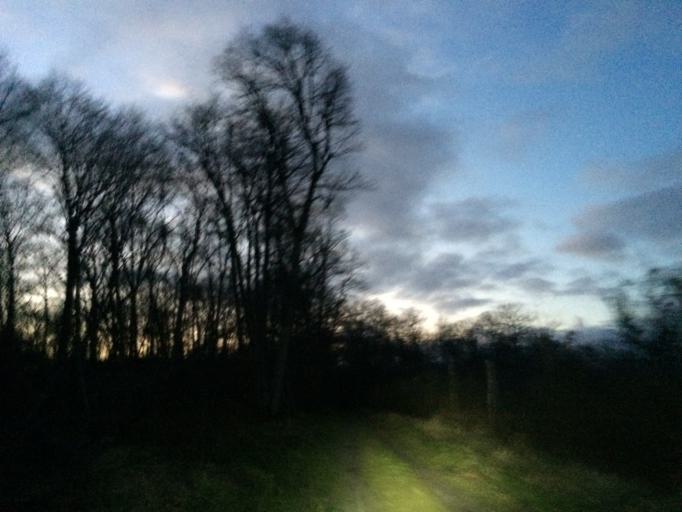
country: FR
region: Picardie
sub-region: Departement de l'Oise
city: Coye-la-Foret
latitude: 49.1494
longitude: 2.4855
